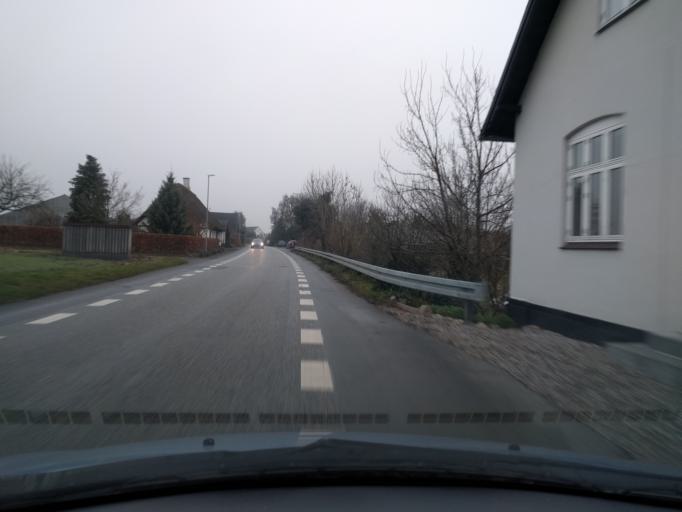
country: DK
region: South Denmark
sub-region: Odense Kommune
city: Bullerup
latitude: 55.3946
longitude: 10.5159
